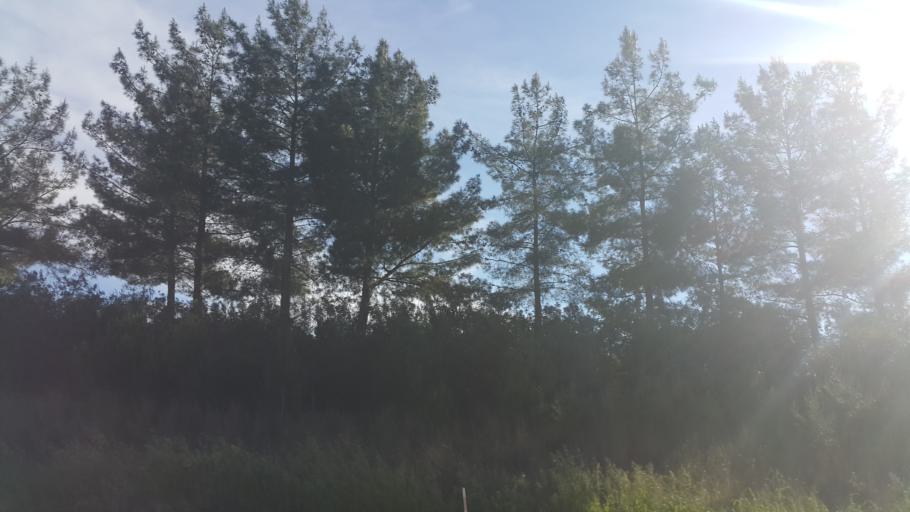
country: TR
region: Adana
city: Yakapinar
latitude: 37.0089
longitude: 35.5108
